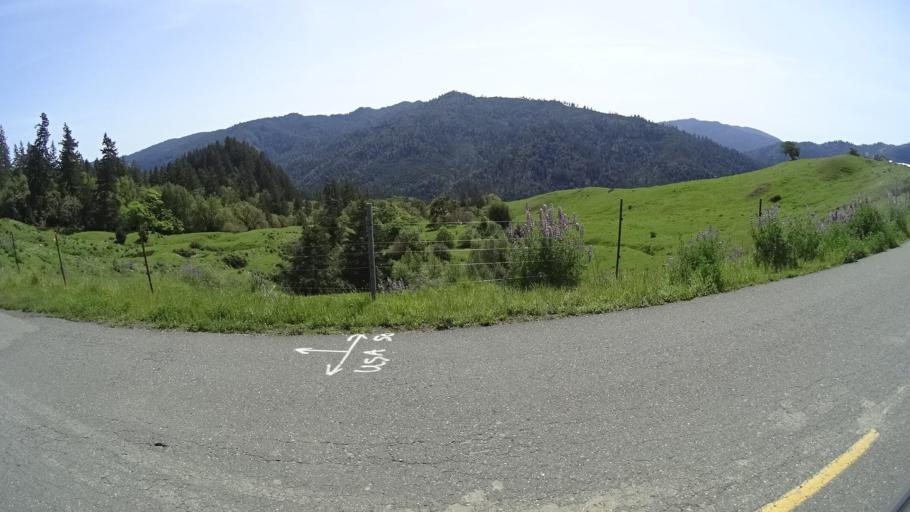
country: US
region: California
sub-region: Humboldt County
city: Redway
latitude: 40.4059
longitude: -123.7477
